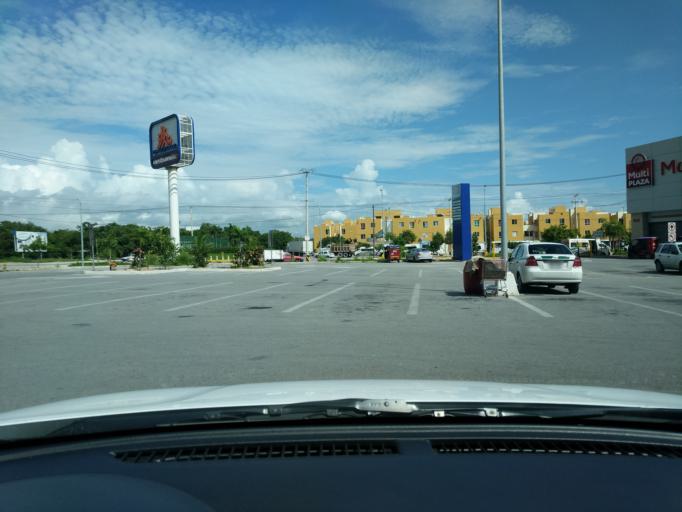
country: MX
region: Quintana Roo
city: Cancun
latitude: 21.1760
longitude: -86.9138
